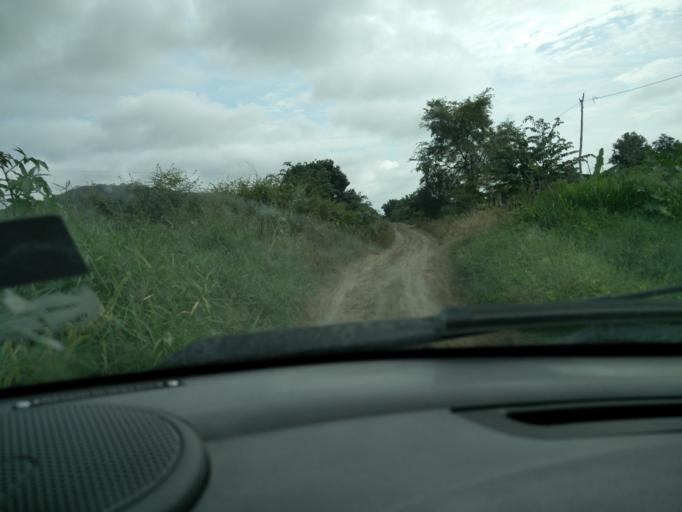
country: EC
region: Manabi
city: Rocafuerte
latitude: -0.8610
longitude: -80.5137
